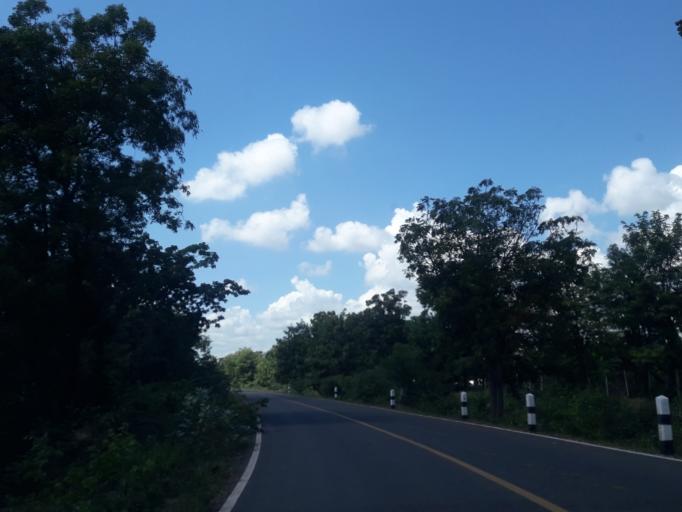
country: TH
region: Lop Buri
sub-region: Amphoe Tha Luang
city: Tha Luang
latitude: 15.0525
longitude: 101.0239
